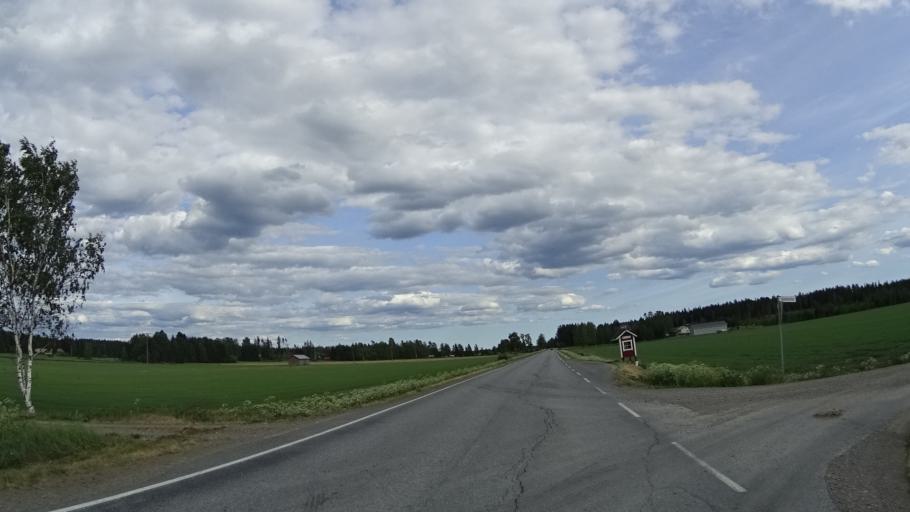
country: FI
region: Pirkanmaa
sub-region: Etelae-Pirkanmaa
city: Urjala
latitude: 60.9438
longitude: 23.5494
